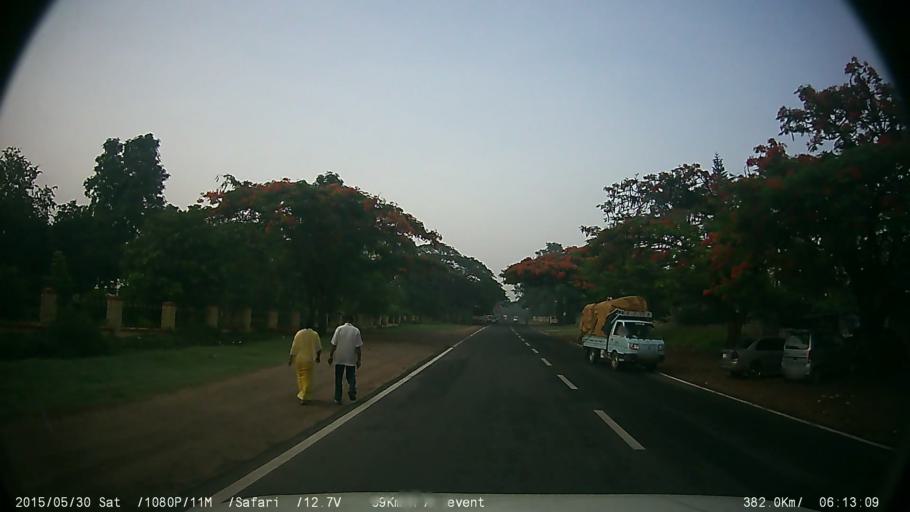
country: IN
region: Karnataka
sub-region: Mysore
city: Mysore
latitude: 12.3371
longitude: 76.6578
